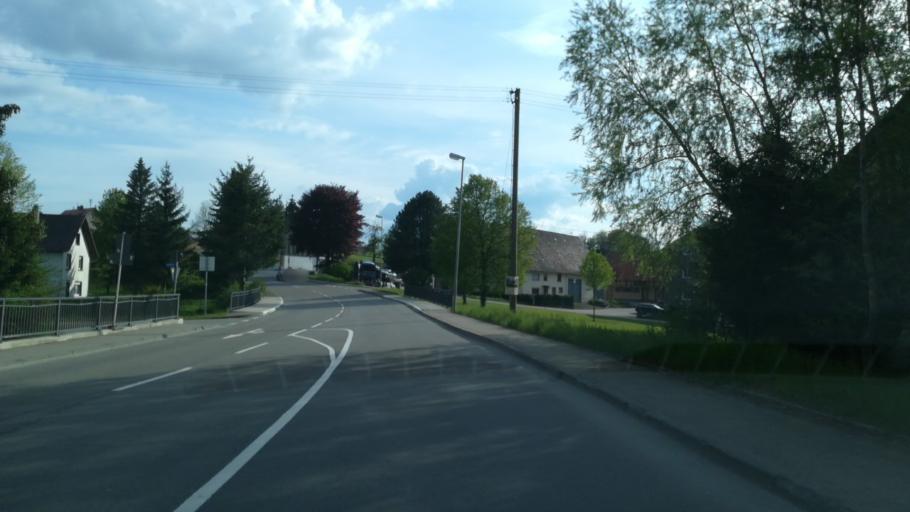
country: DE
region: Baden-Wuerttemberg
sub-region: Freiburg Region
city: Muhlingen
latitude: 47.9620
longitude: 9.0451
